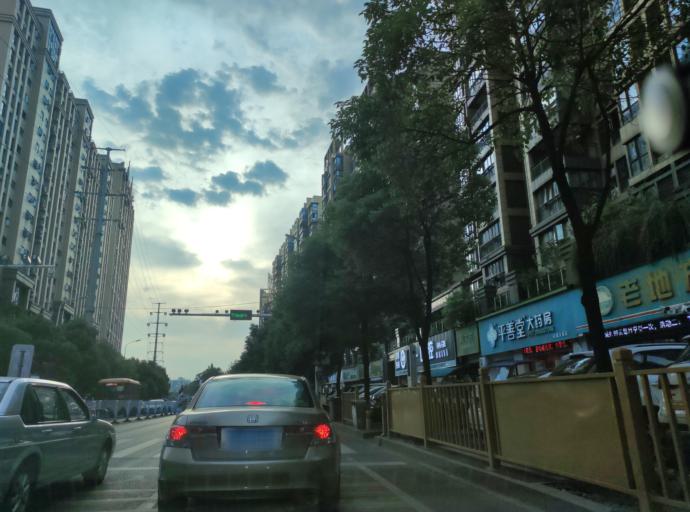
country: CN
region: Jiangxi Sheng
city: Pingxiang
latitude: 27.6336
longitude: 113.8668
